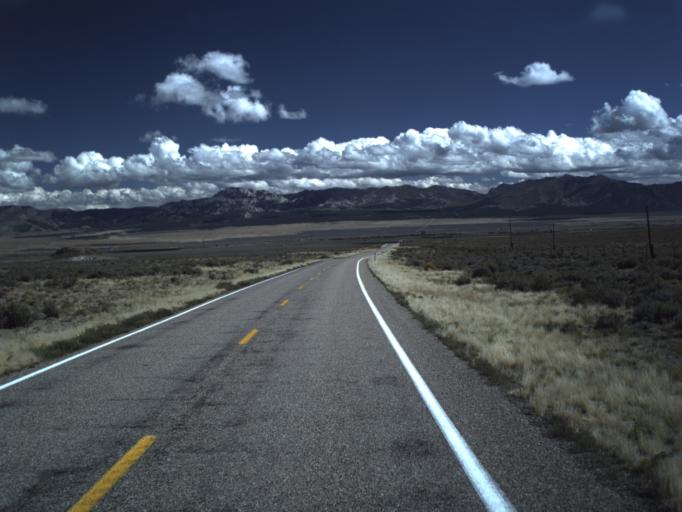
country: US
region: Utah
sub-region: Beaver County
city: Milford
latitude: 38.4236
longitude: -113.1097
